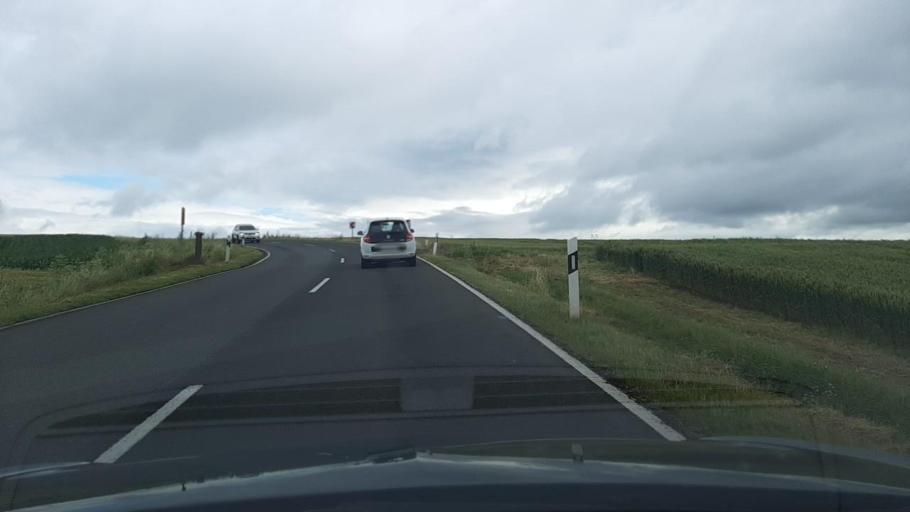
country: DE
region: Rheinland-Pfalz
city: Kerben
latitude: 50.3177
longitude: 7.3862
